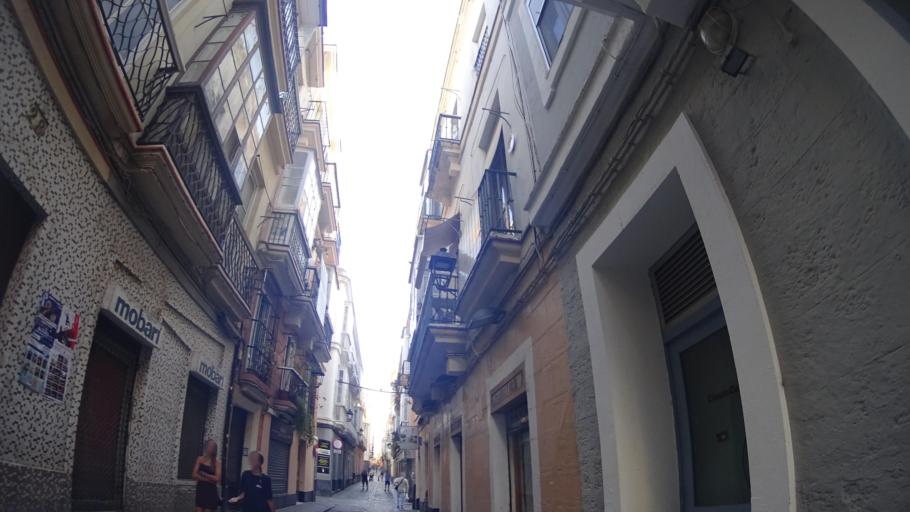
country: ES
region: Andalusia
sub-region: Provincia de Cadiz
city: Cadiz
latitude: 36.5336
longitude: -6.2993
